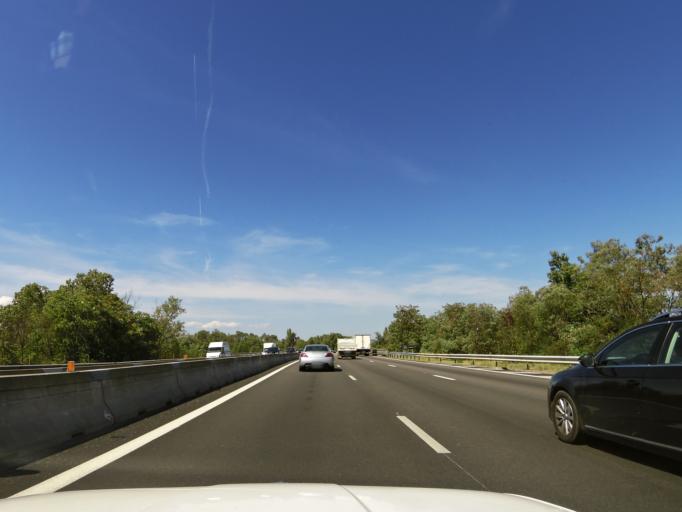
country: FR
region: Rhone-Alpes
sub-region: Departement de la Drome
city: La Roche-de-Glun
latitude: 44.9969
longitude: 4.8776
